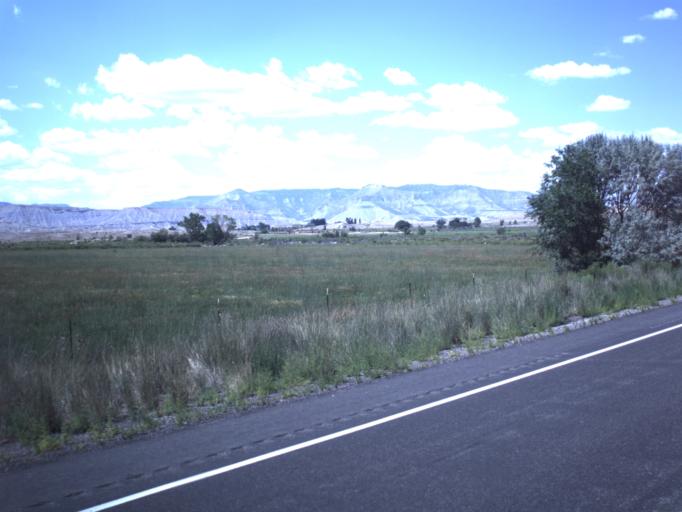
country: US
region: Utah
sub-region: Emery County
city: Huntington
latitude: 39.2661
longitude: -110.9806
